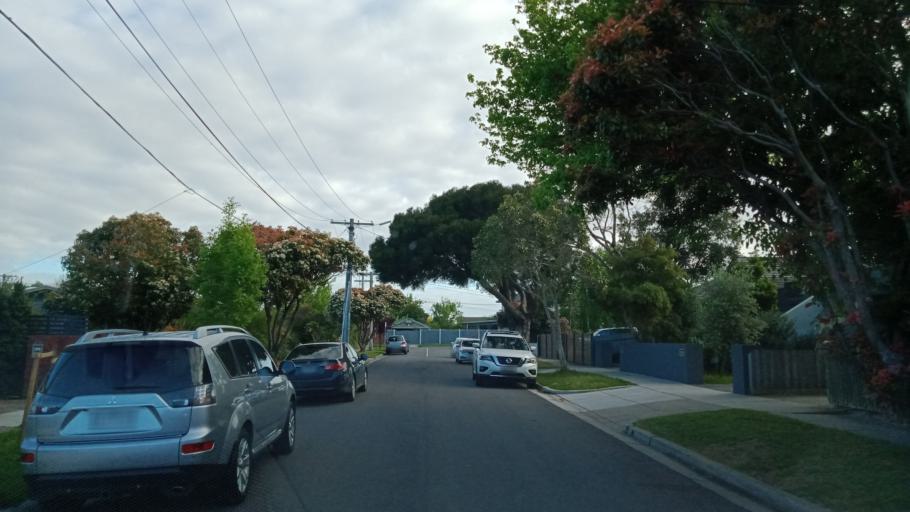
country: AU
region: Victoria
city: McKinnon
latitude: -37.9324
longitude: 145.0525
